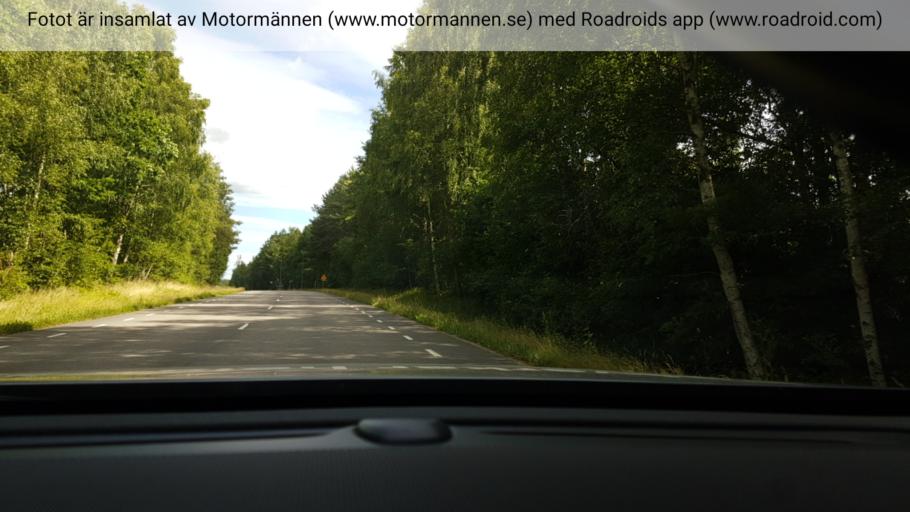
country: SE
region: Skane
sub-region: Hassleholms Kommun
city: Hassleholm
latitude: 56.1766
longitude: 13.7869
